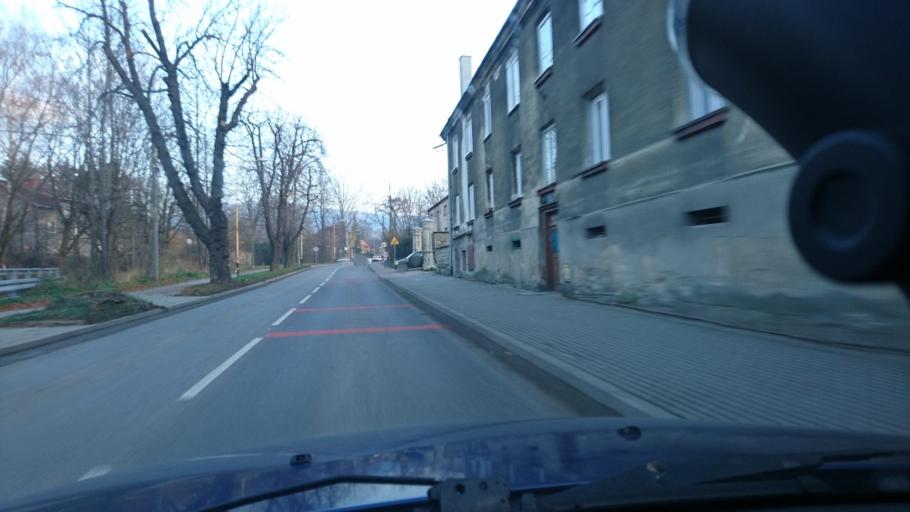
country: PL
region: Silesian Voivodeship
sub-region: Bielsko-Biala
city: Bielsko-Biala
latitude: 49.8184
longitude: 19.0643
